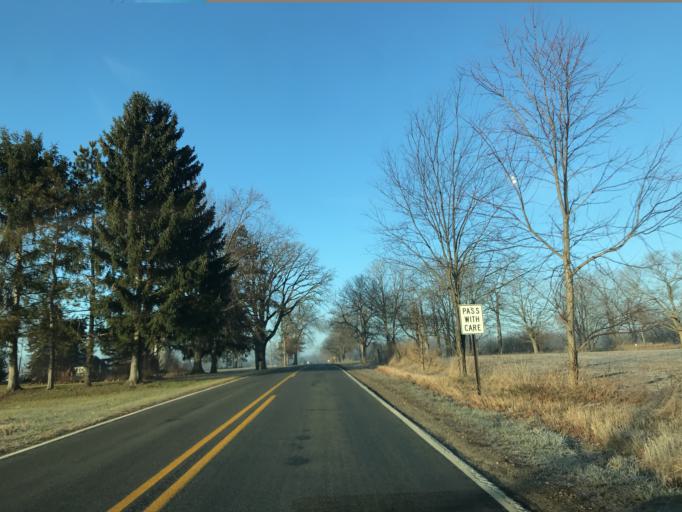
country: US
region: Michigan
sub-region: Eaton County
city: Eaton Rapids
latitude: 42.4511
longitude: -84.5755
